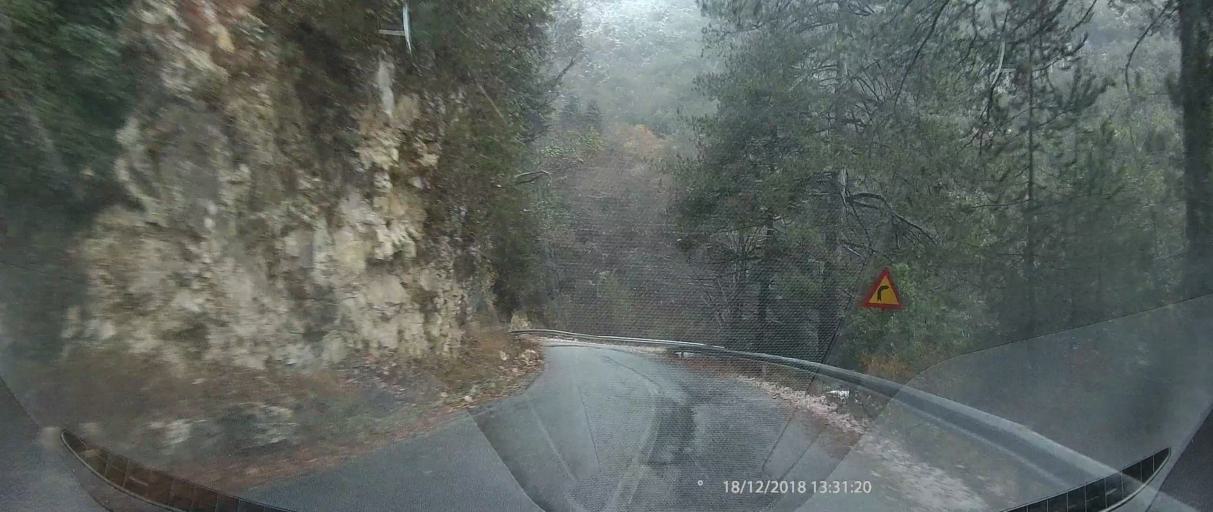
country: GR
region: Central Macedonia
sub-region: Nomos Pierias
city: Litochoro
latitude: 40.1111
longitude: 22.4773
